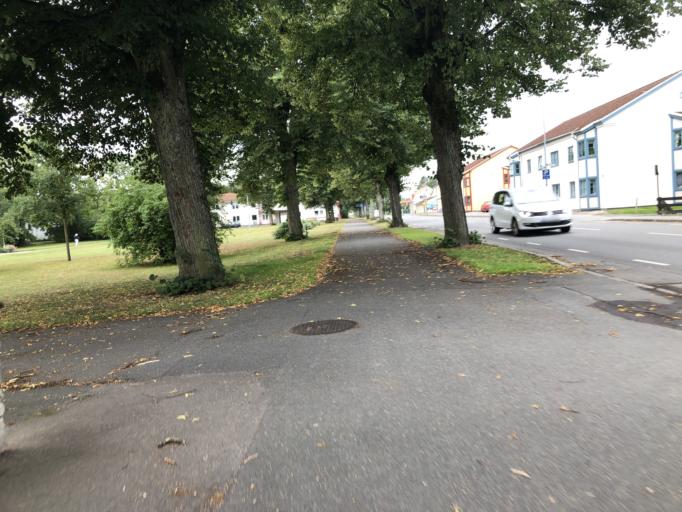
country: SE
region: Skane
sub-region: Hassleholms Kommun
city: Vinslov
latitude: 56.1047
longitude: 13.9132
